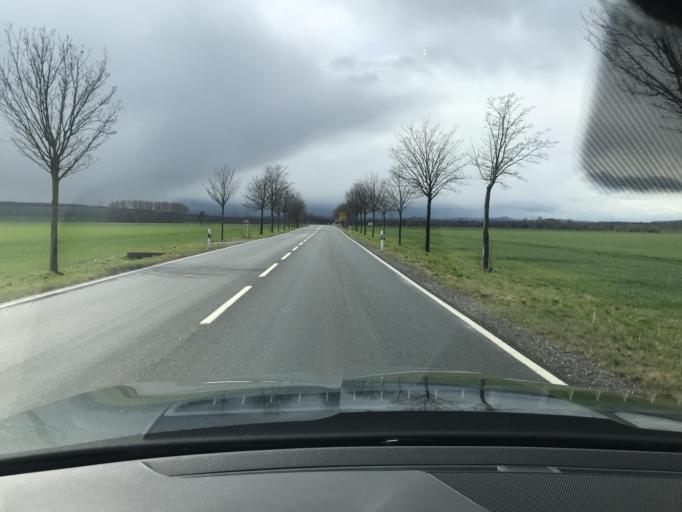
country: DE
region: Saxony-Anhalt
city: Gatersleben
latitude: 51.7862
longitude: 11.2586
